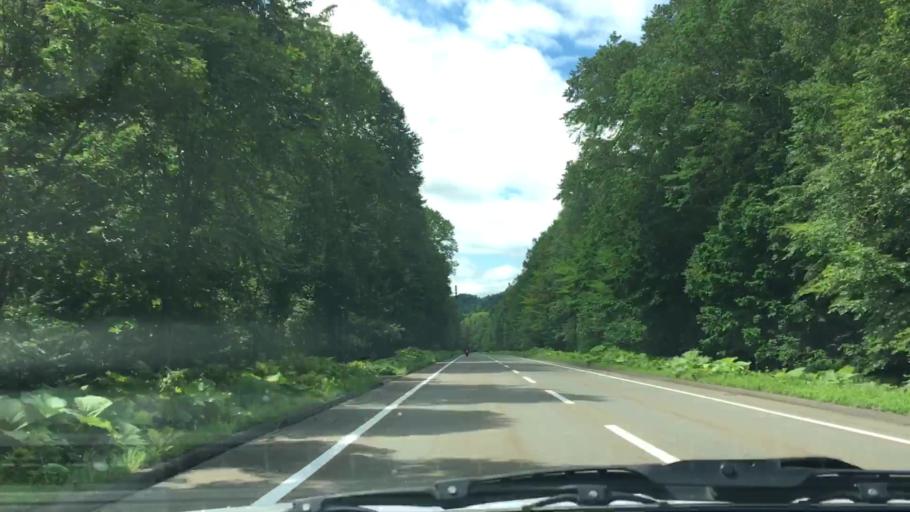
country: JP
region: Hokkaido
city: Kitami
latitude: 43.4016
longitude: 143.9303
